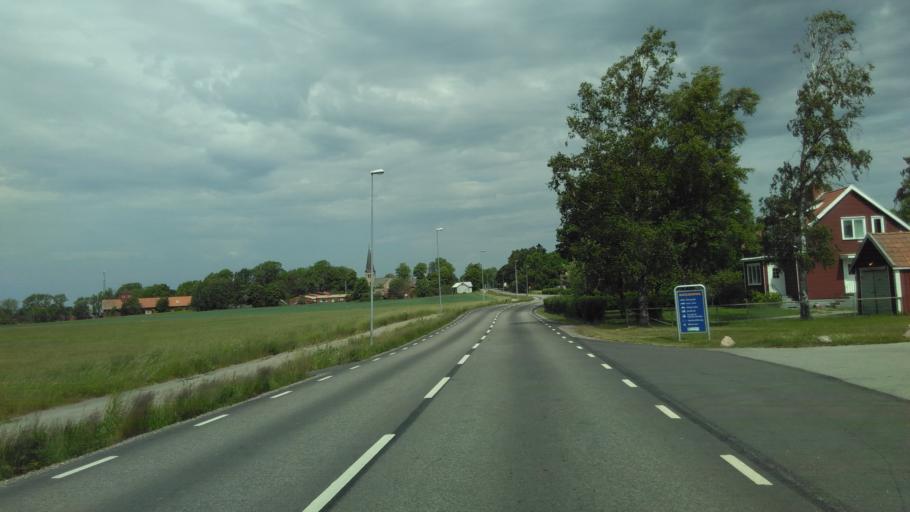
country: SE
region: Vaestra Goetaland
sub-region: Vara Kommun
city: Kvanum
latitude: 58.3761
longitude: 13.1478
